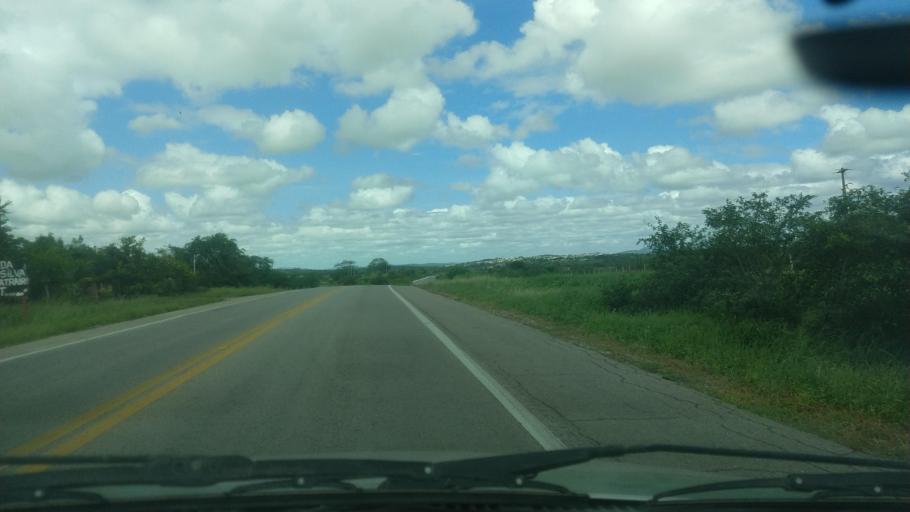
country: BR
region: Rio Grande do Norte
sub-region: Tangara
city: Tangara
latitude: -6.1806
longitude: -35.7717
